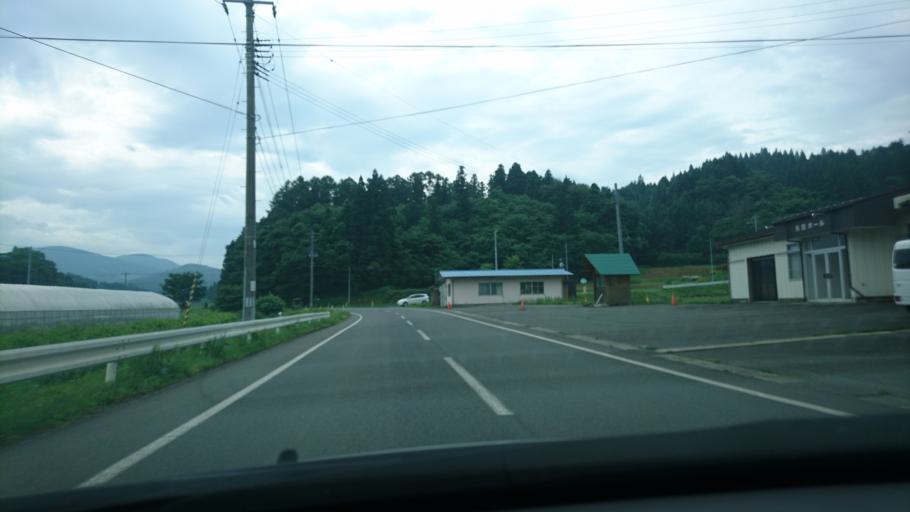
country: JP
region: Iwate
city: Ichinoseki
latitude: 38.9117
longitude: 141.4190
